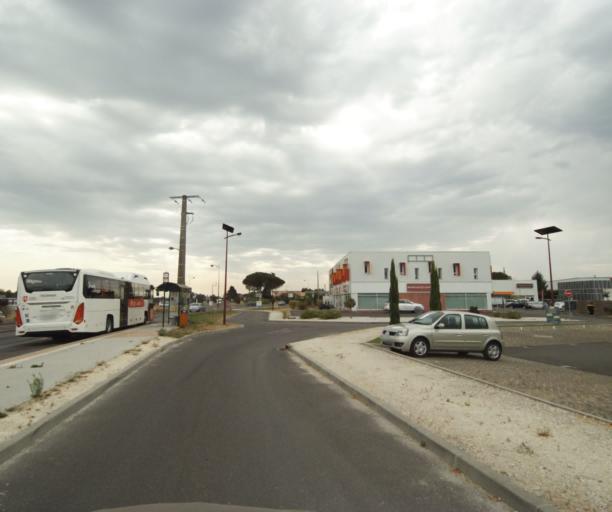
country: FR
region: Aquitaine
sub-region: Departement de la Gironde
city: Creon
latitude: 44.7721
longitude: -0.3375
